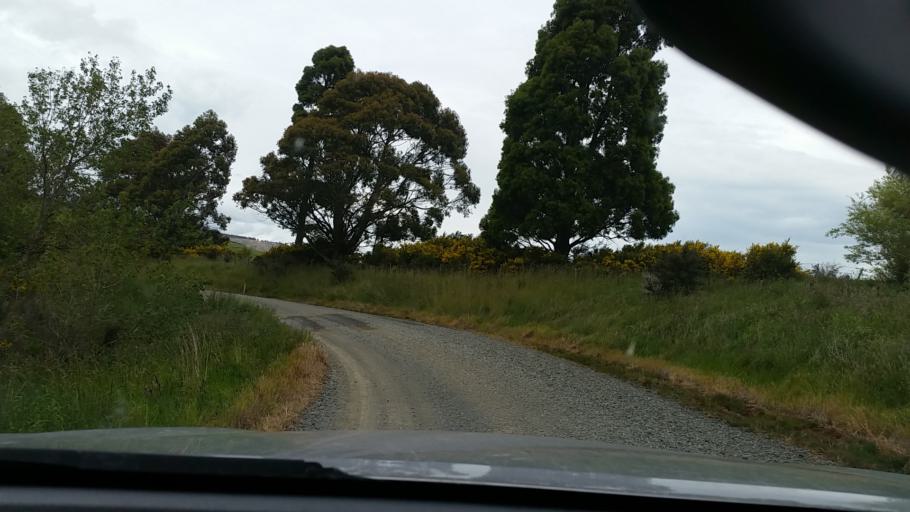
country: NZ
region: Southland
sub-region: Southland District
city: Winton
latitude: -45.8298
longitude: 168.1605
